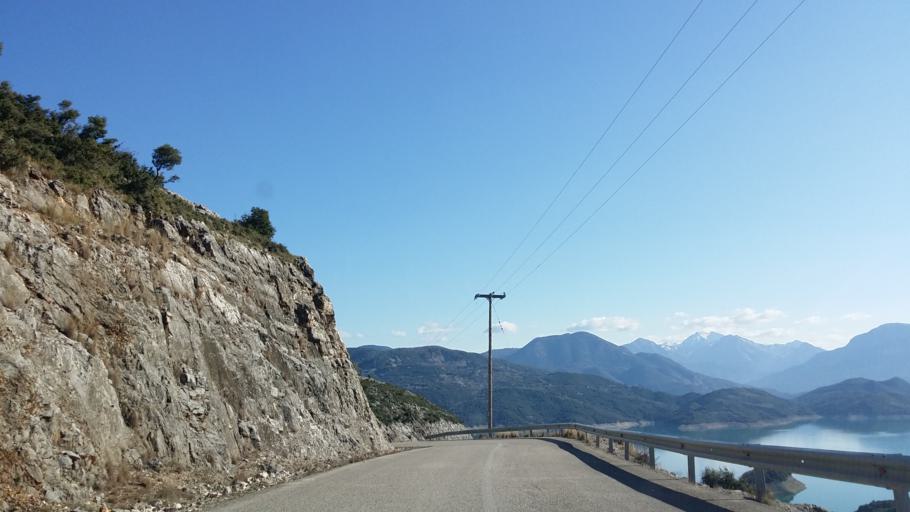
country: GR
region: Central Greece
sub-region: Nomos Evrytanias
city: Kerasochori
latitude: 38.9652
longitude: 21.4708
